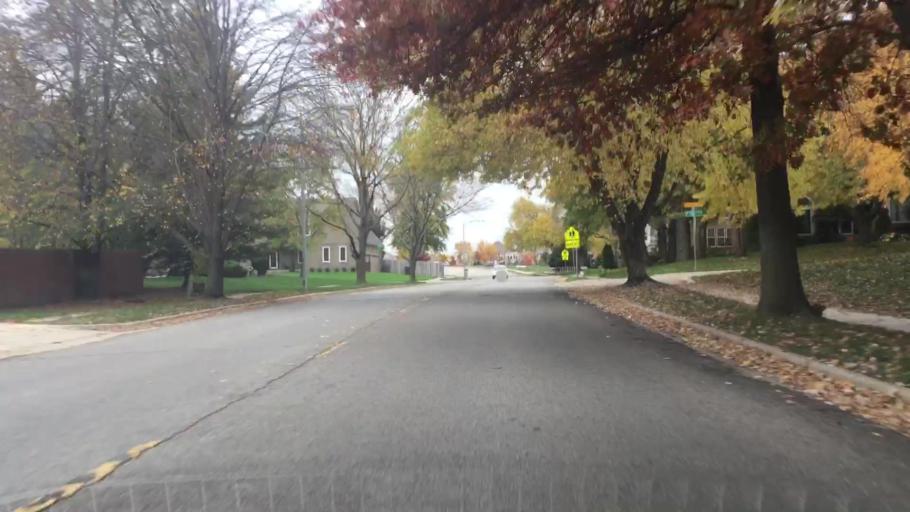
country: US
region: Kansas
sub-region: Johnson County
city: Lenexa
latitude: 38.9215
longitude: -94.7493
